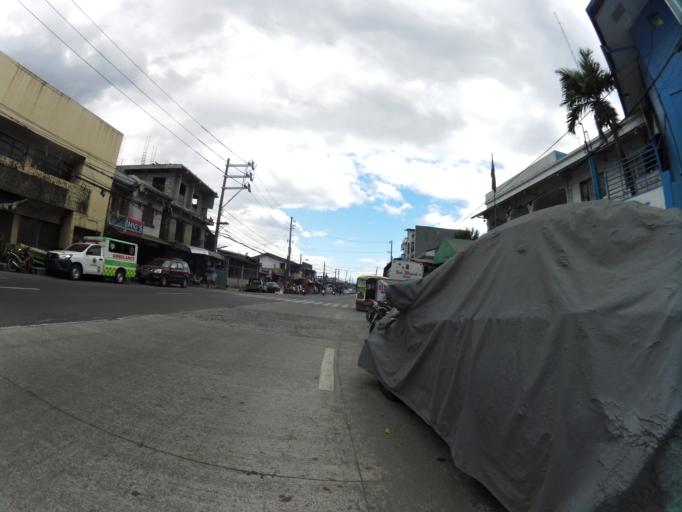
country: PH
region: Calabarzon
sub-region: Province of Rizal
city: Antipolo
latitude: 14.6297
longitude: 121.1202
